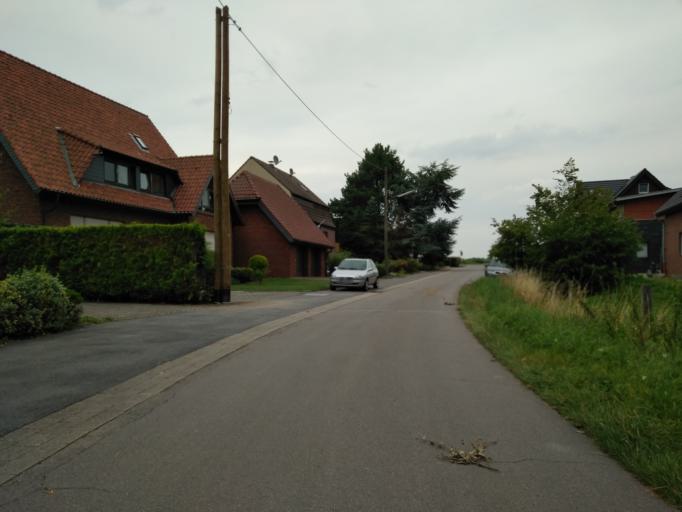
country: DE
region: North Rhine-Westphalia
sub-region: Regierungsbezirk Munster
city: Bottrop
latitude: 51.5963
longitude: 6.9084
